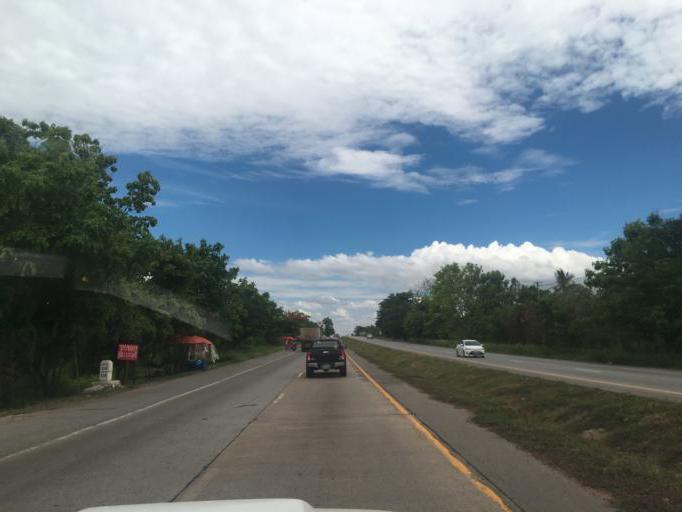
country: TH
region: Khon Kaen
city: Nam Phong
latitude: 16.6489
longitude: 102.8002
